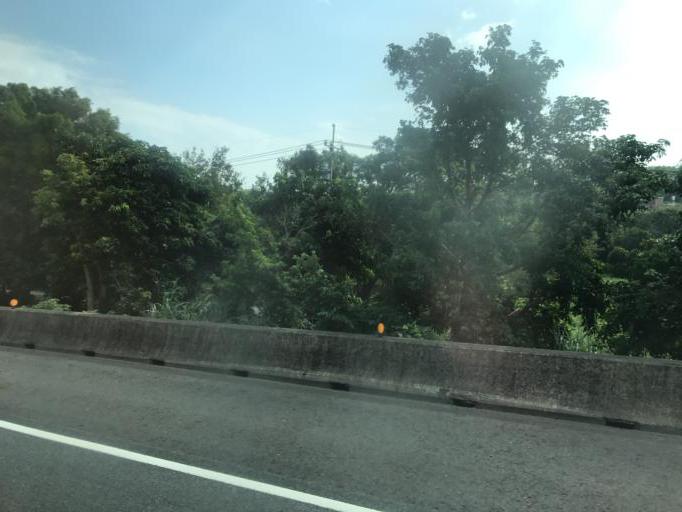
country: TW
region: Taiwan
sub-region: Hsinchu
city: Zhubei
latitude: 24.8761
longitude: 121.0528
